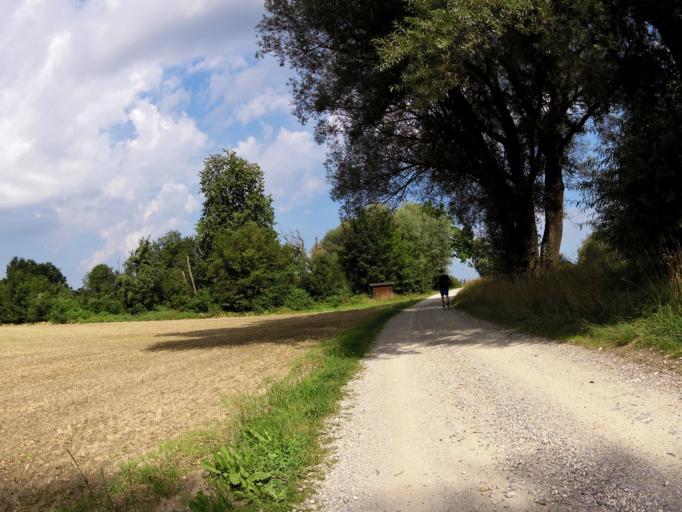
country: DE
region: Bavaria
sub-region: Upper Bavaria
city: Pahl
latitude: 47.9226
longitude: 11.1462
